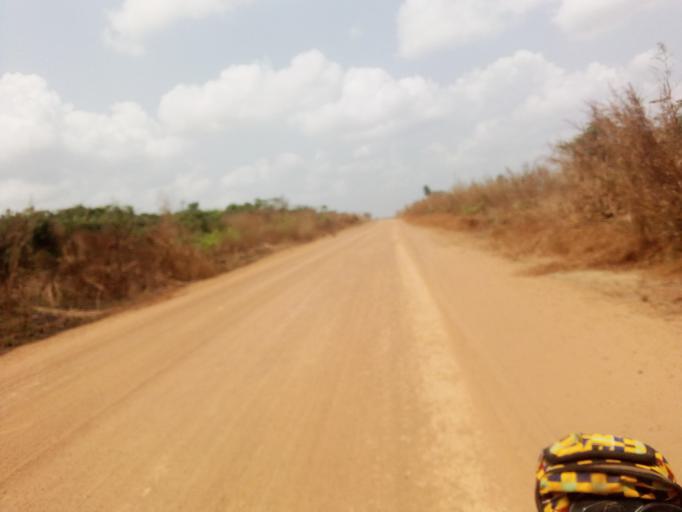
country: SL
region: Southern Province
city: Mogbwemo
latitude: 7.6609
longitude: -12.2675
